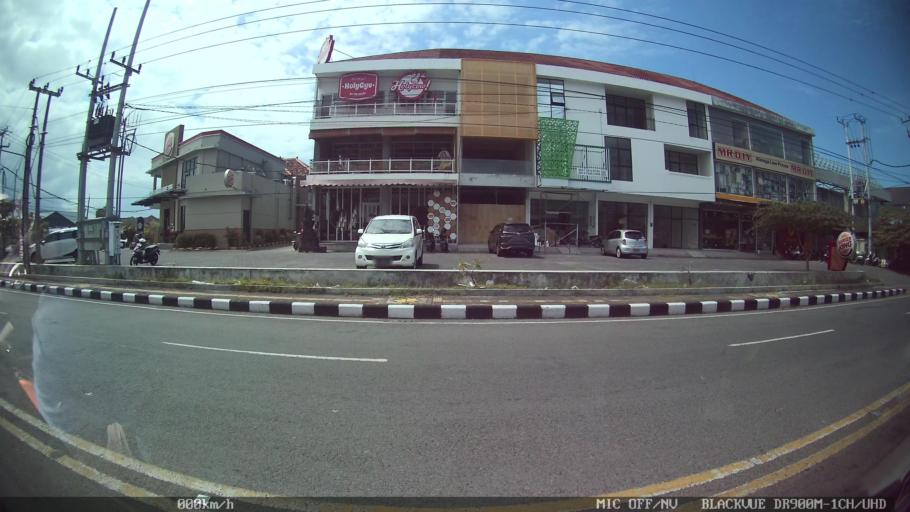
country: ID
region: Bali
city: Karyadharma
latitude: -8.6816
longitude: 115.1892
